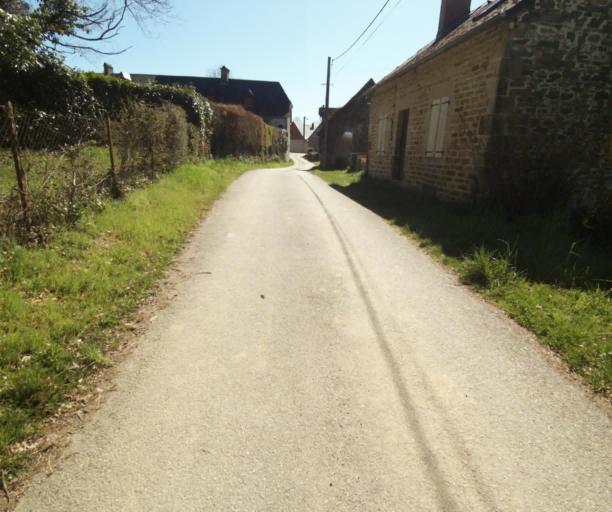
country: FR
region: Limousin
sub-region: Departement de la Correze
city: Chamboulive
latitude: 45.4280
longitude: 1.7208
